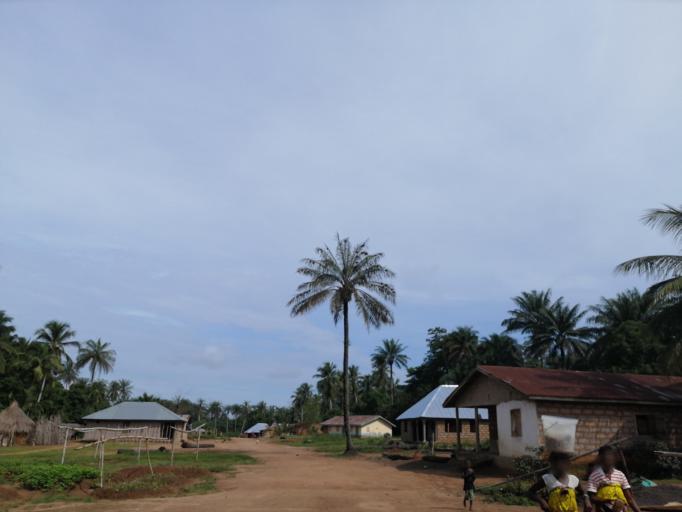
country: SL
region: Northern Province
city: Port Loko
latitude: 8.7909
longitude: -12.9331
